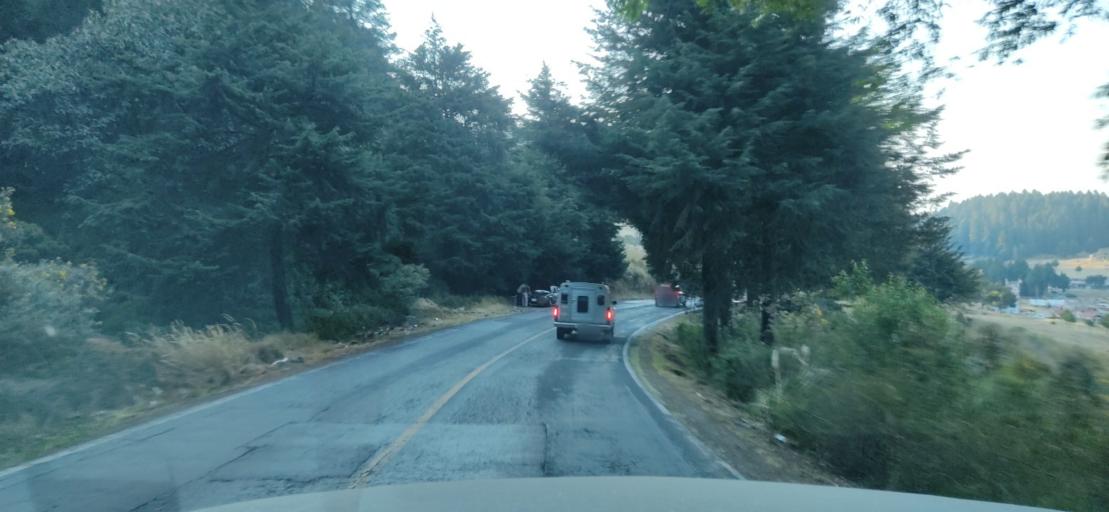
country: MX
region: Mexico
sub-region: Ocoyoacac
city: San Jeronimo Acazulco
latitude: 19.2755
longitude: -99.3787
